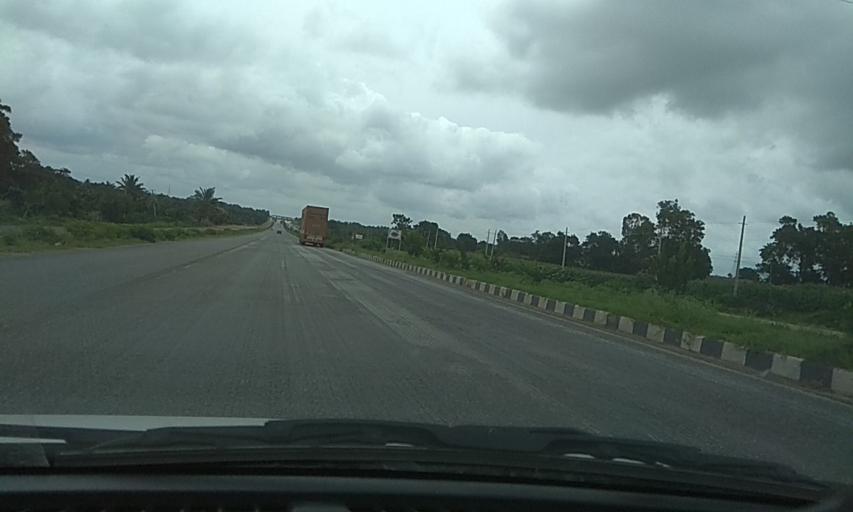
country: IN
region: Karnataka
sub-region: Davanagere
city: Mayakonda
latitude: 14.3693
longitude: 76.1368
